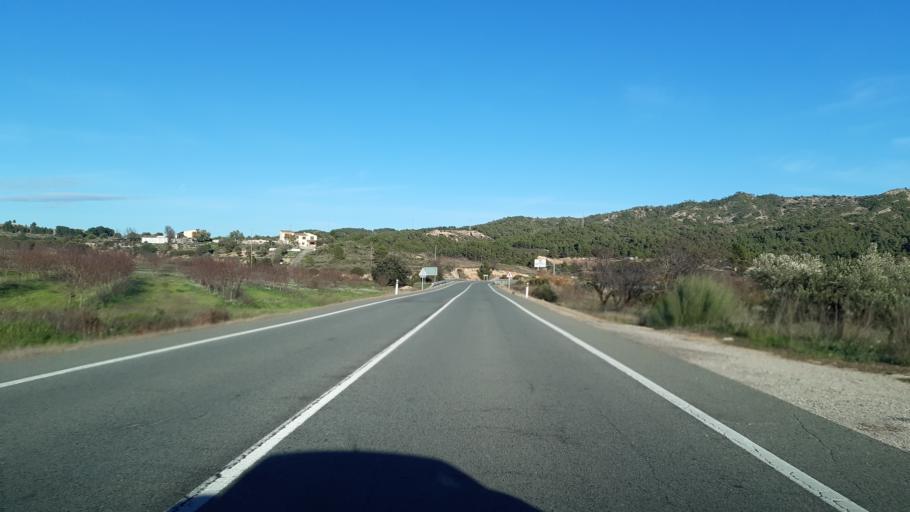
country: ES
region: Catalonia
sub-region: Provincia de Tarragona
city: la Fatarella
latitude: 41.1090
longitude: 0.5303
